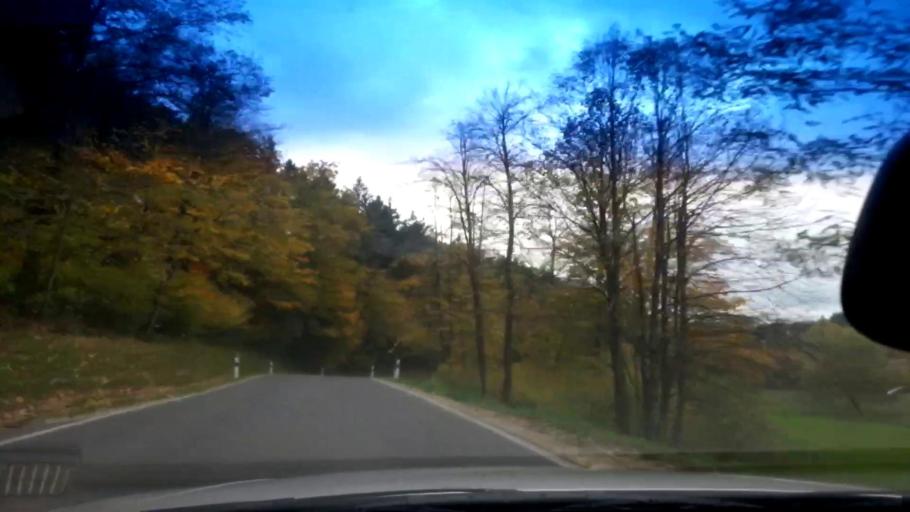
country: DE
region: Bavaria
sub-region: Upper Franconia
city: Wonsees
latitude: 49.9952
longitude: 11.2981
